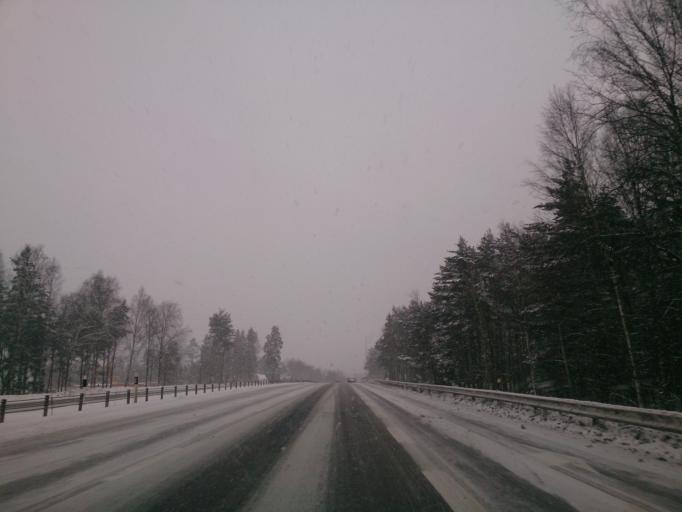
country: SE
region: Soedermanland
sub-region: Nykopings Kommun
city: Nykoping
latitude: 58.7626
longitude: 16.9897
